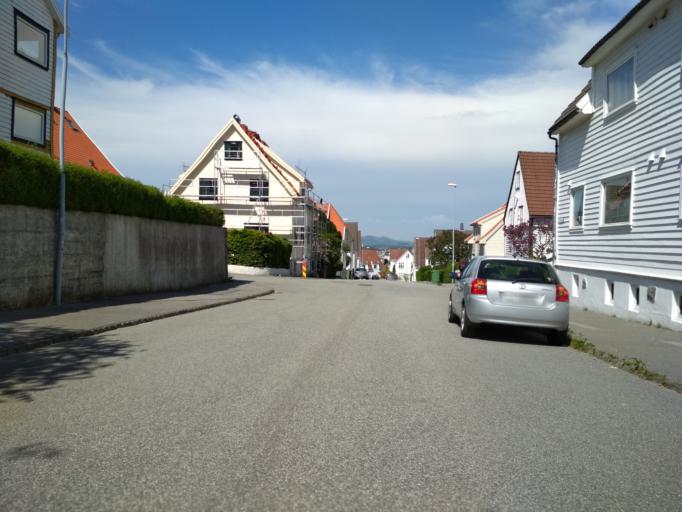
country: NO
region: Rogaland
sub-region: Stavanger
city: Stavanger
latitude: 58.9575
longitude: 5.7336
